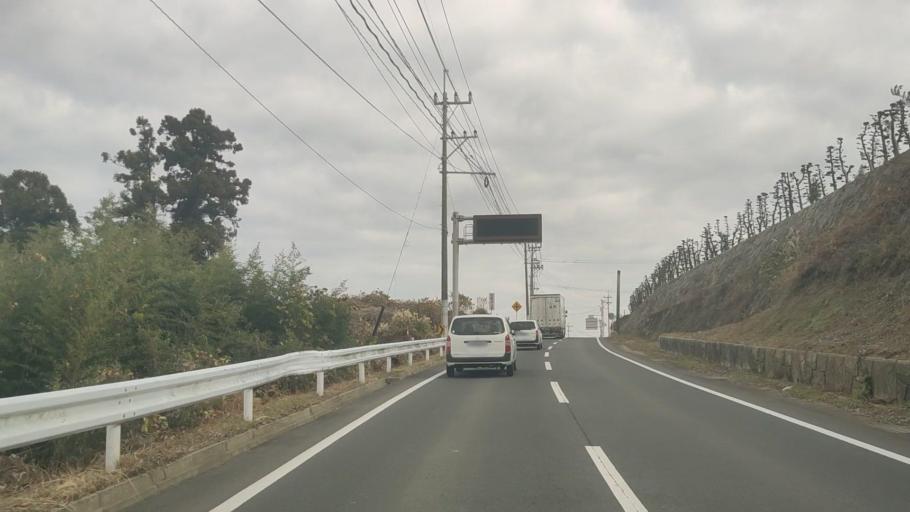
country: JP
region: Nagasaki
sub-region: Isahaya-shi
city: Isahaya
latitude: 32.8166
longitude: 130.1746
